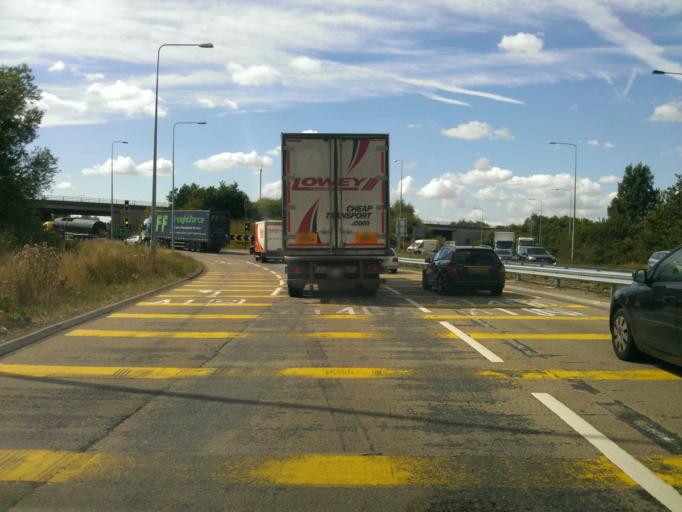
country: GB
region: England
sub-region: Cambridgeshire
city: Brampton
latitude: 52.3322
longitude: -0.2459
